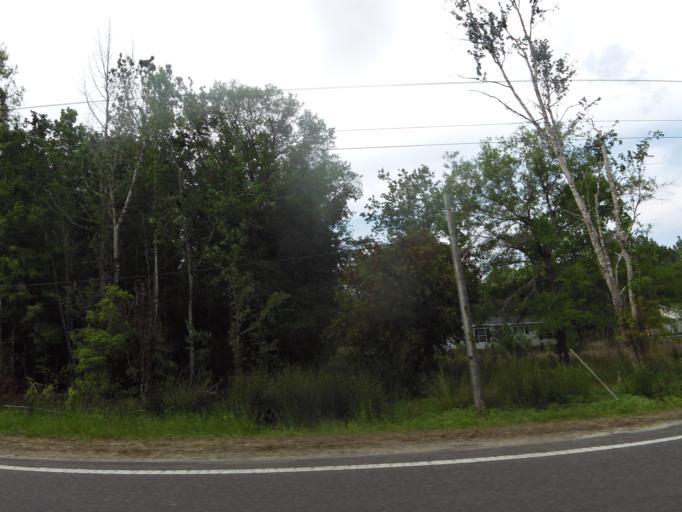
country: US
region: Florida
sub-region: Nassau County
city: Hilliard
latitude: 30.6983
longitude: -81.8919
